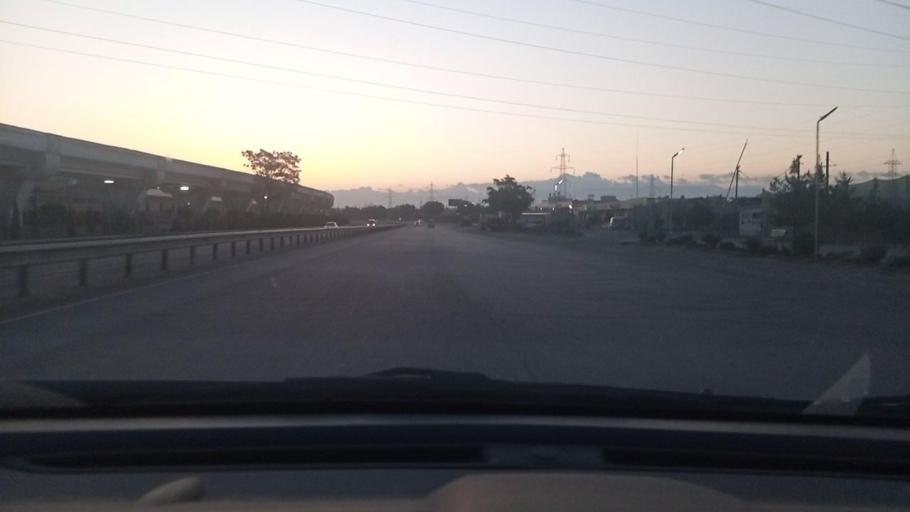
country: UZ
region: Toshkent Shahri
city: Bektemir
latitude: 41.2454
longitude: 69.3442
